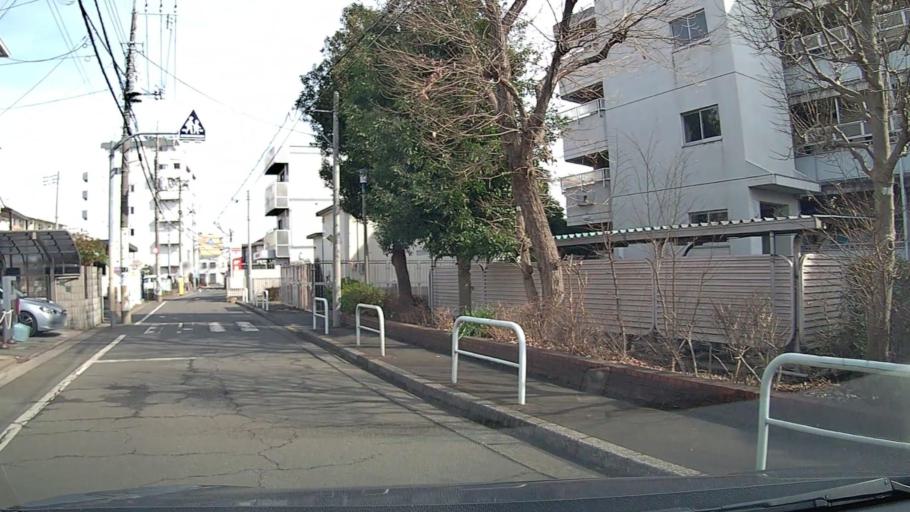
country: JP
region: Tokyo
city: Tanashicho
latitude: 35.7524
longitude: 139.5582
